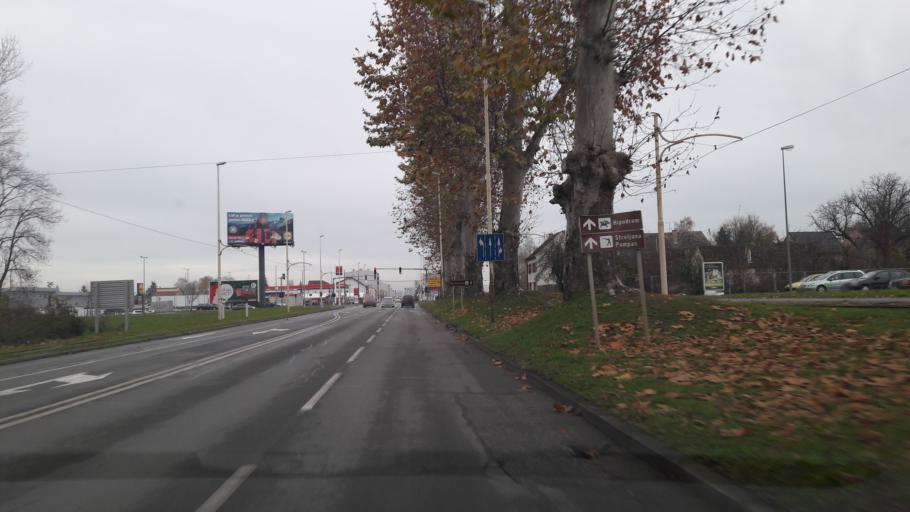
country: HR
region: Osjecko-Baranjska
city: Visnjevac
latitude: 45.5652
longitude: 18.6343
